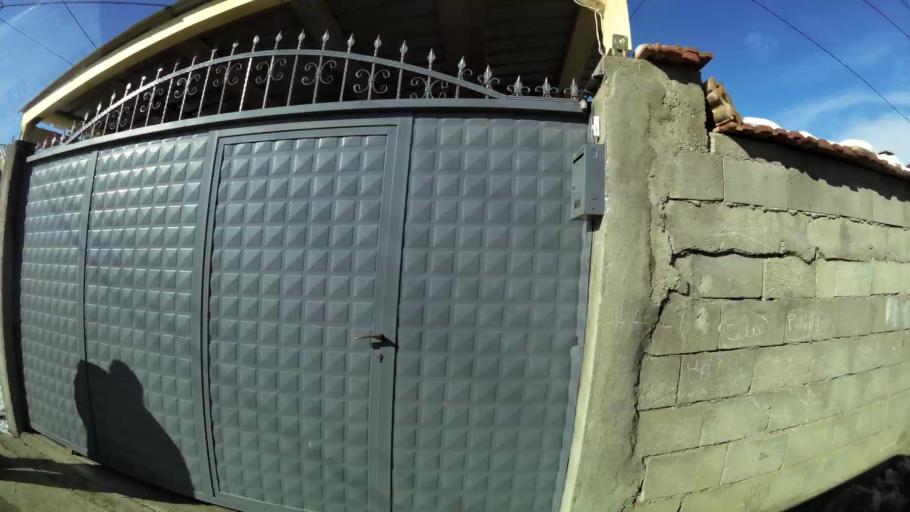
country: MK
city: Ljubin
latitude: 41.9969
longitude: 21.3180
